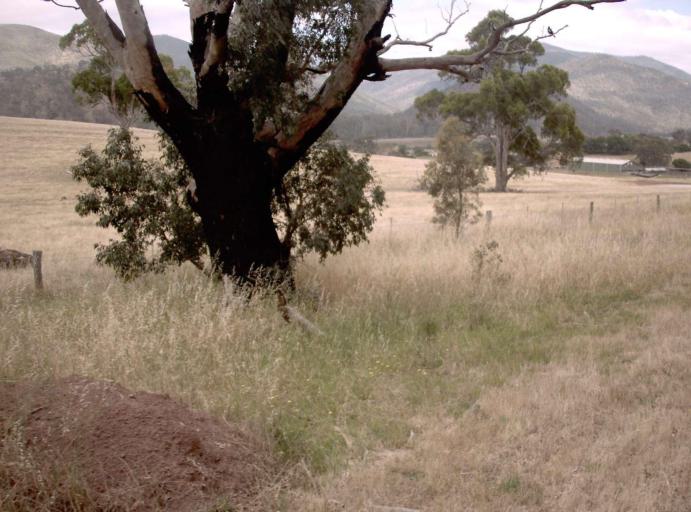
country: AU
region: Victoria
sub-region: Wellington
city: Heyfield
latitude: -37.6746
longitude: 146.6541
